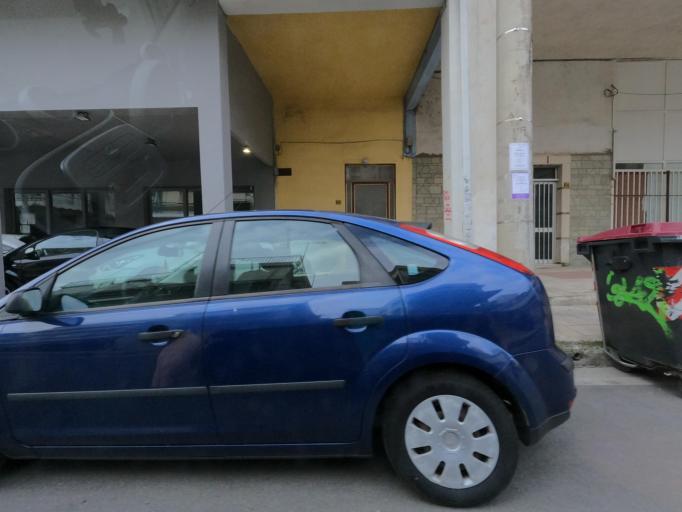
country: GR
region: Attica
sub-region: Nomarchia Athinas
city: Peristeri
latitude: 38.0157
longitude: 23.6793
